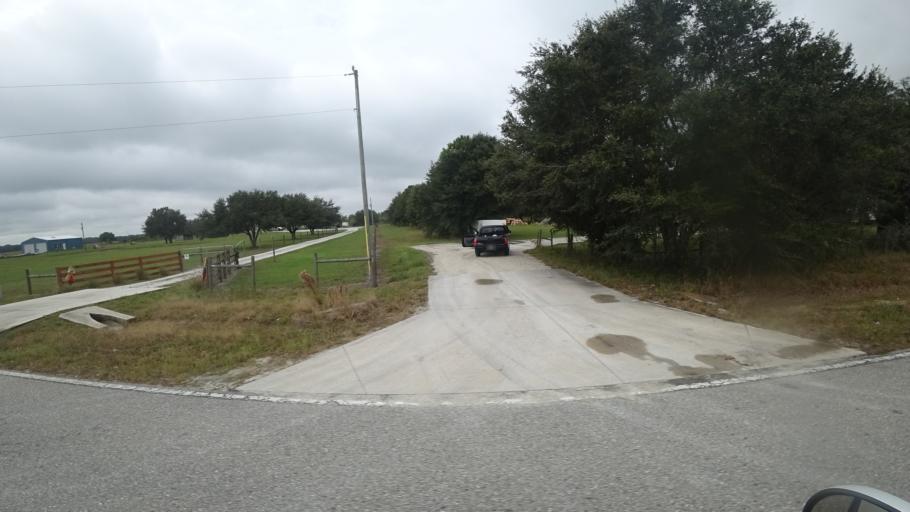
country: US
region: Florida
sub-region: Sarasota County
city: Warm Mineral Springs
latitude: 27.2758
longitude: -82.1961
